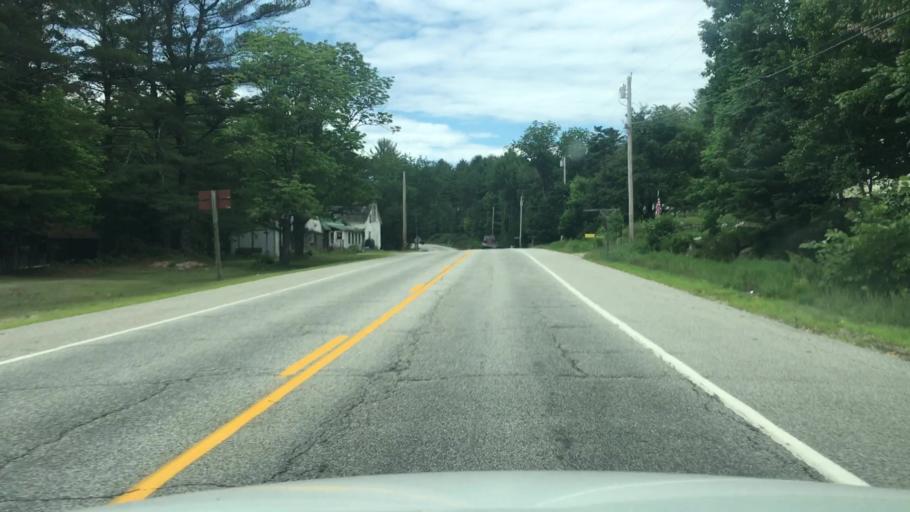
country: US
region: Maine
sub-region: Oxford County
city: West Paris
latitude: 44.3362
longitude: -70.5568
